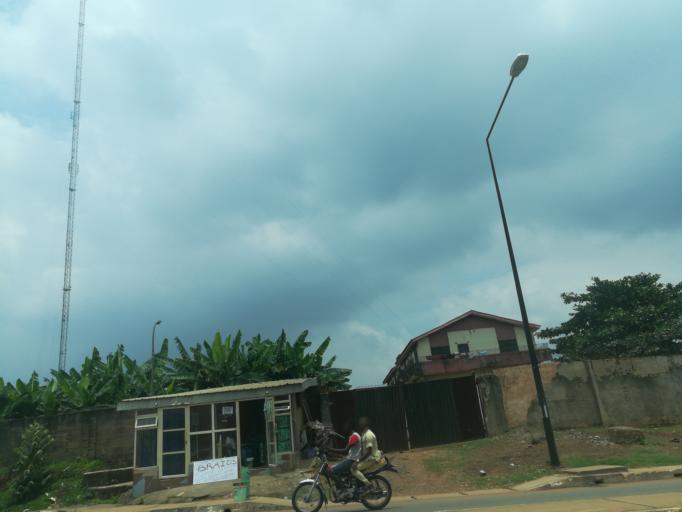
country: NG
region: Lagos
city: Ikorodu
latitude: 6.6282
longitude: 3.5306
